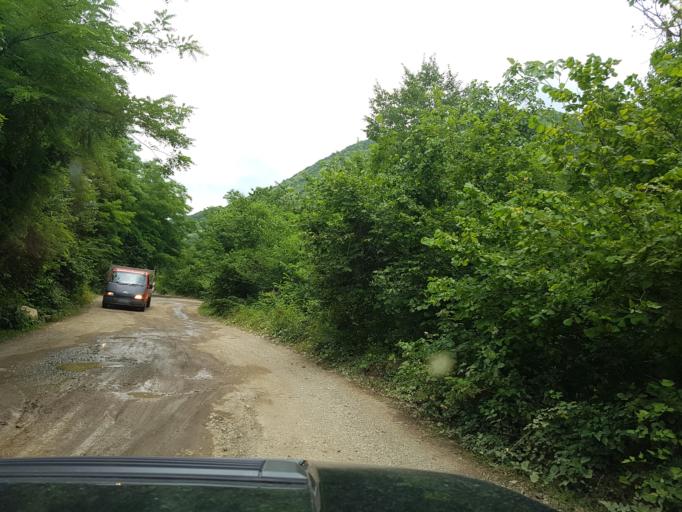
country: GE
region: Imereti
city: Kutaisi
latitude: 42.4246
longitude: 42.7432
